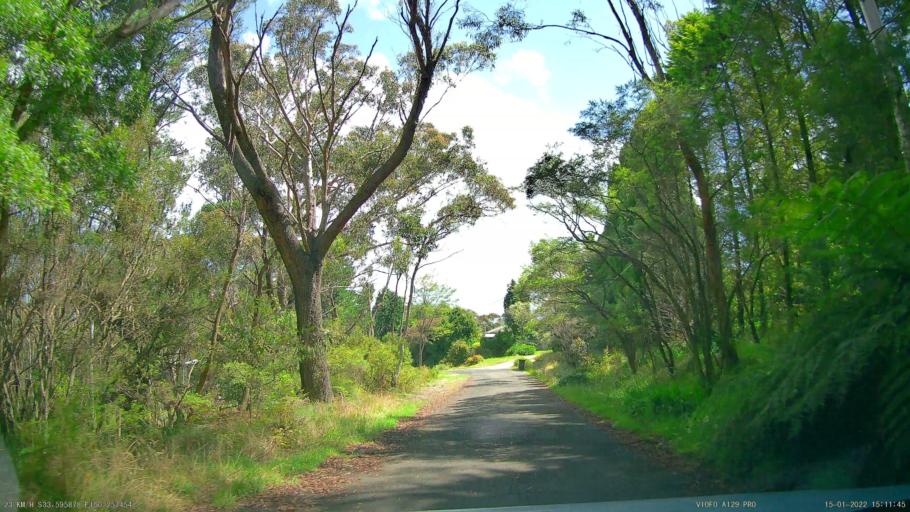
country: AU
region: New South Wales
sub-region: Blue Mountains Municipality
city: Blackheath
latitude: -33.5960
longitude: 150.2574
